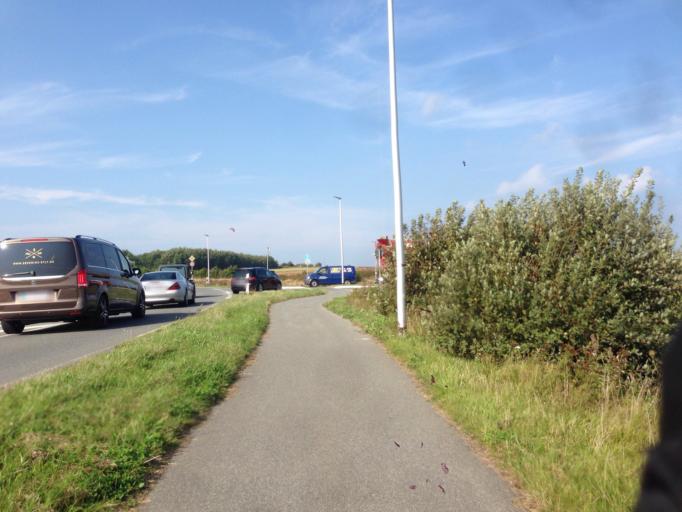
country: DE
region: Schleswig-Holstein
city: Keitum
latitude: 54.8956
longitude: 8.3605
